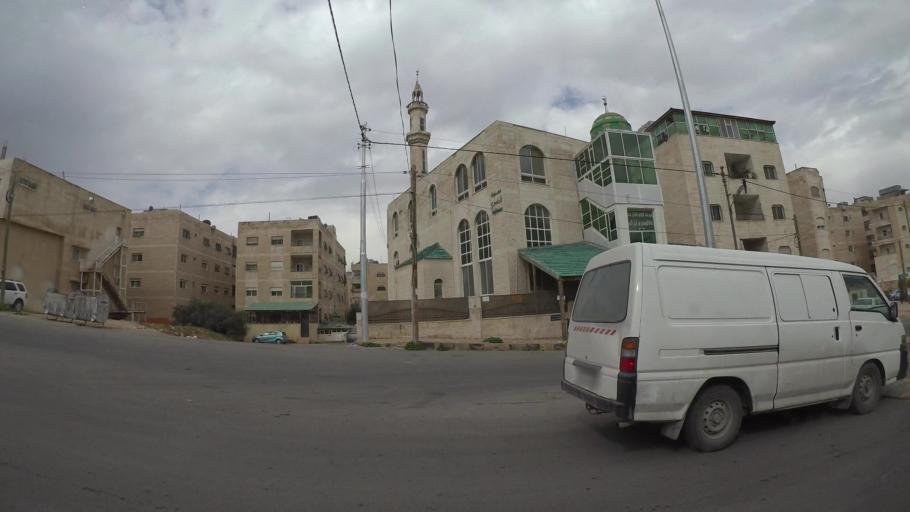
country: JO
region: Amman
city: Amman
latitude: 31.9786
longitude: 35.9304
